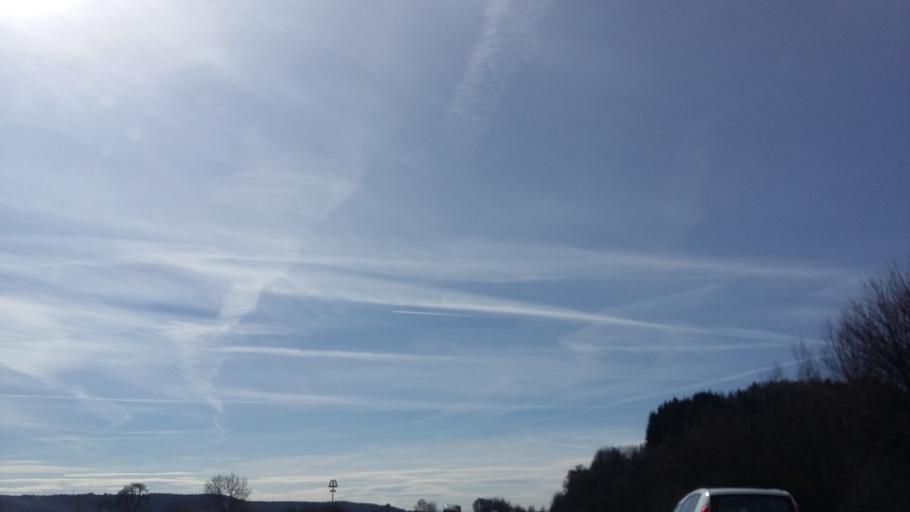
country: DE
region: Baden-Wuerttemberg
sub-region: Tuebingen Region
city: Aichstetten
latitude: 47.8834
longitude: 10.0396
